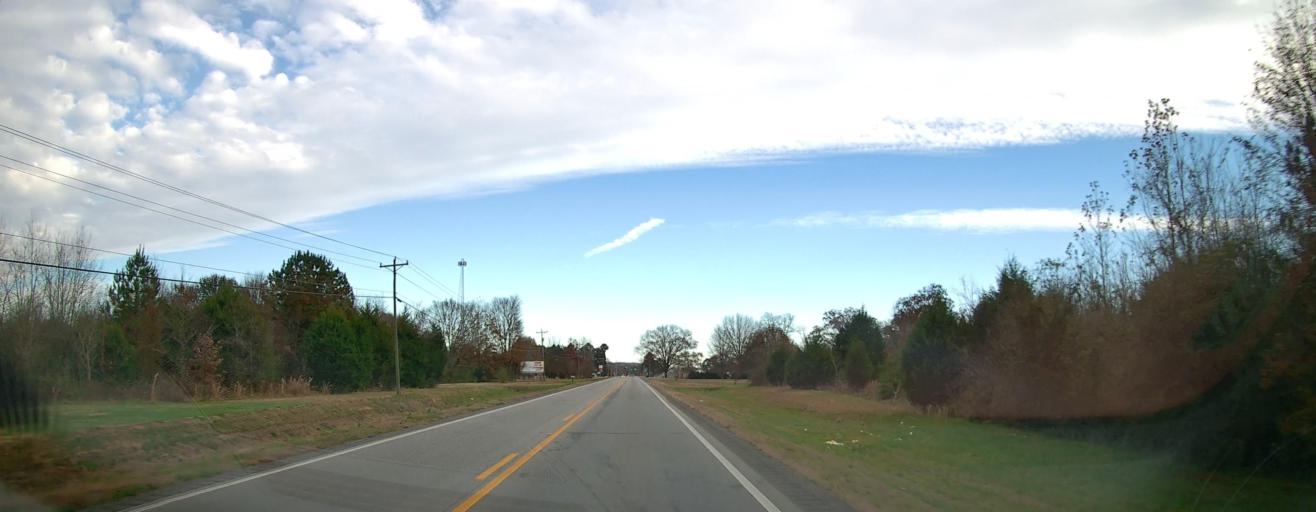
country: US
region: Alabama
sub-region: Morgan County
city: Falkville
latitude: 34.4184
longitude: -86.7090
